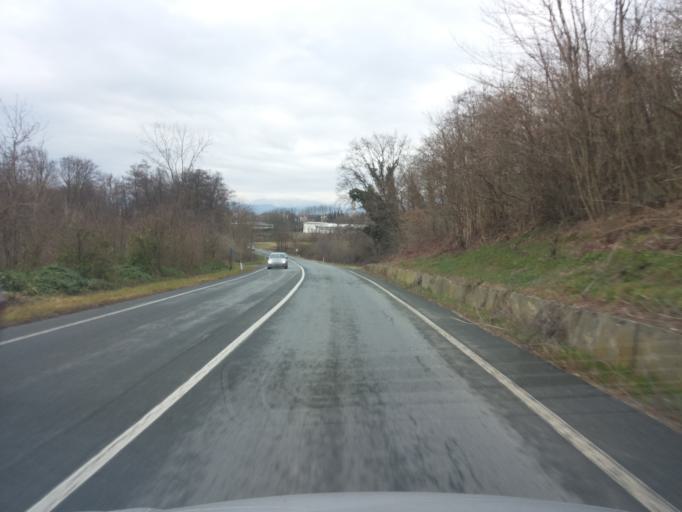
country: IT
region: Piedmont
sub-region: Provincia di Torino
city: Vestigne
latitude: 45.3818
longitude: 7.9634
